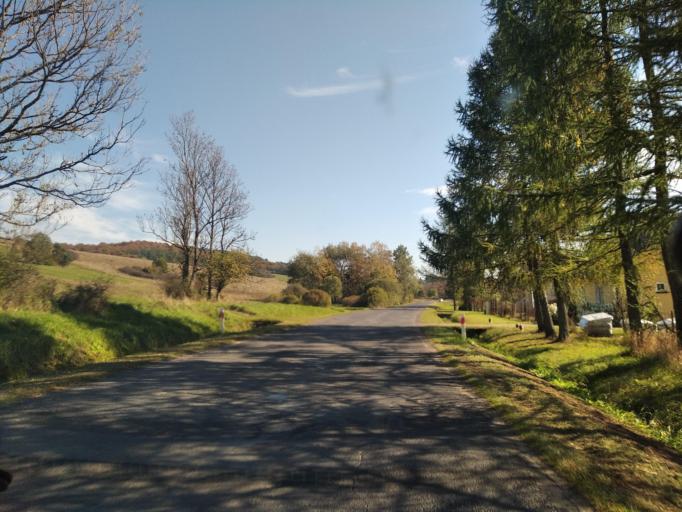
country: PL
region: Subcarpathian Voivodeship
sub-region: Powiat sanocki
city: Bukowsko
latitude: 49.4139
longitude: 21.9745
